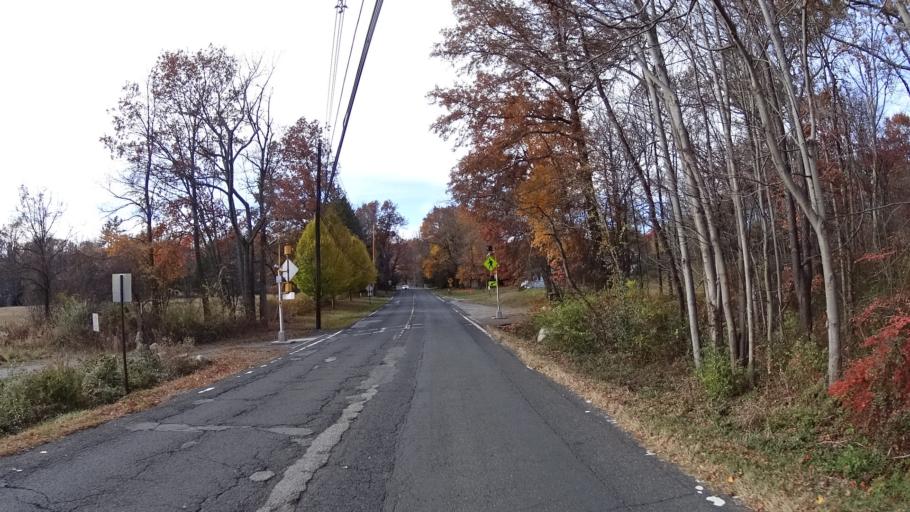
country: US
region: New Jersey
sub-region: Morris County
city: Madison
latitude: 40.7527
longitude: -74.4480
